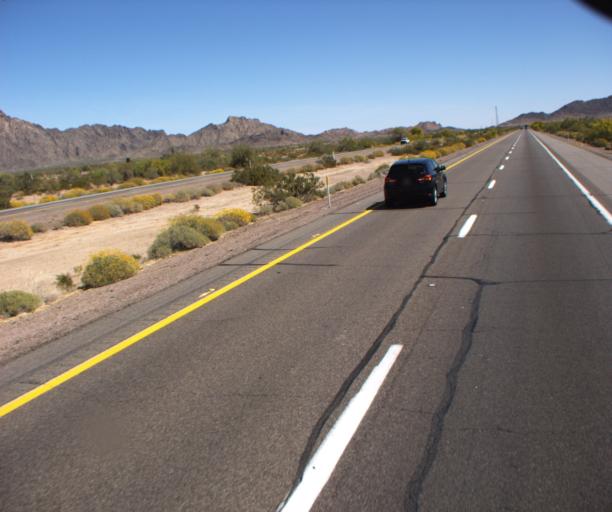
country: US
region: Arizona
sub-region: Yuma County
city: Wellton
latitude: 32.7185
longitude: -113.7874
